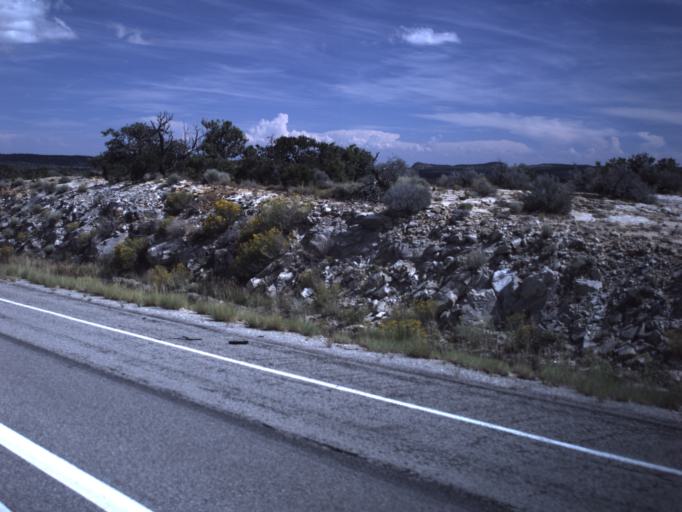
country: US
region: Utah
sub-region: Emery County
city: Ferron
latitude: 38.8657
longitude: -110.8078
